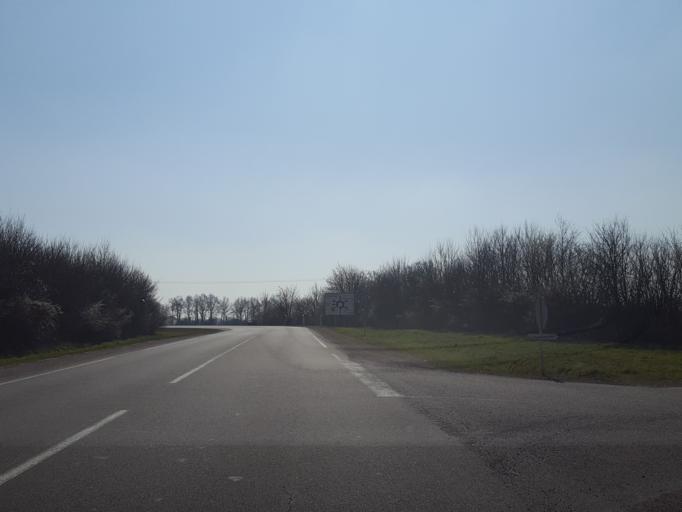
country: FR
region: Pays de la Loire
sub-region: Departement de la Vendee
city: La Chaize-le-Vicomte
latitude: 46.6659
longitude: -1.3436
